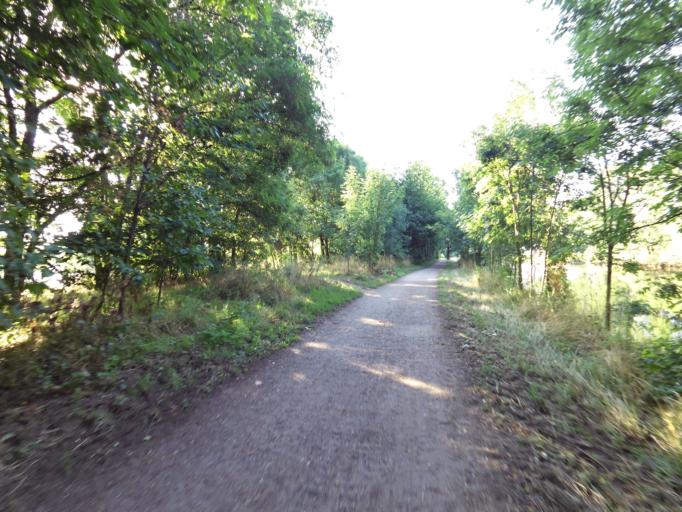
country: DE
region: North Rhine-Westphalia
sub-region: Regierungsbezirk Koln
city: Wassenberg
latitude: 51.0604
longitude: 6.1646
